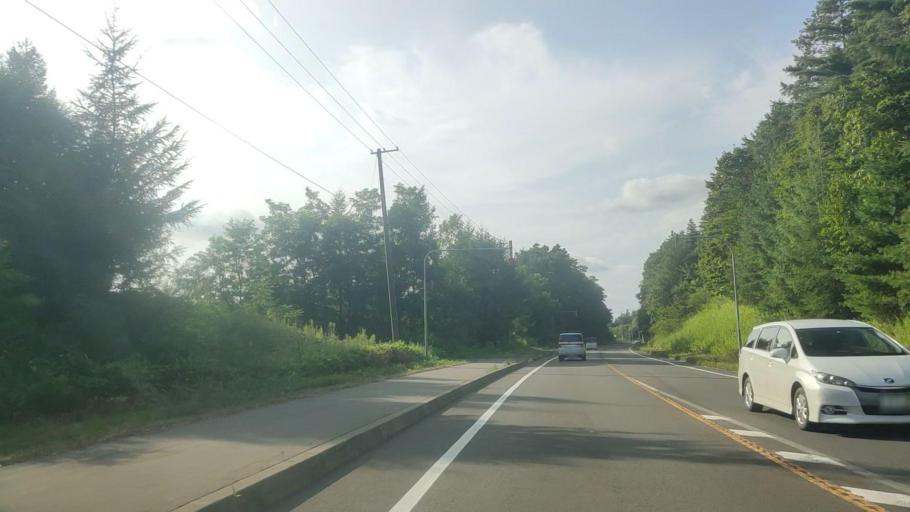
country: JP
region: Hokkaido
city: Chitose
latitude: 42.8778
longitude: 141.8173
